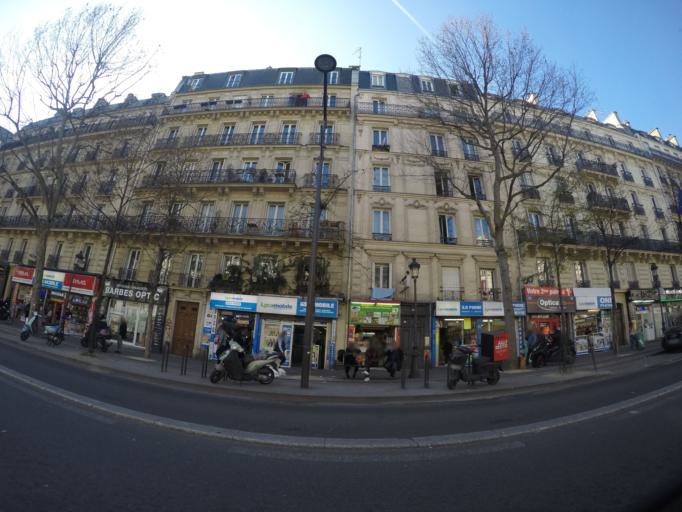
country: FR
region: Ile-de-France
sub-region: Paris
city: Saint-Ouen
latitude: 48.8859
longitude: 2.3499
